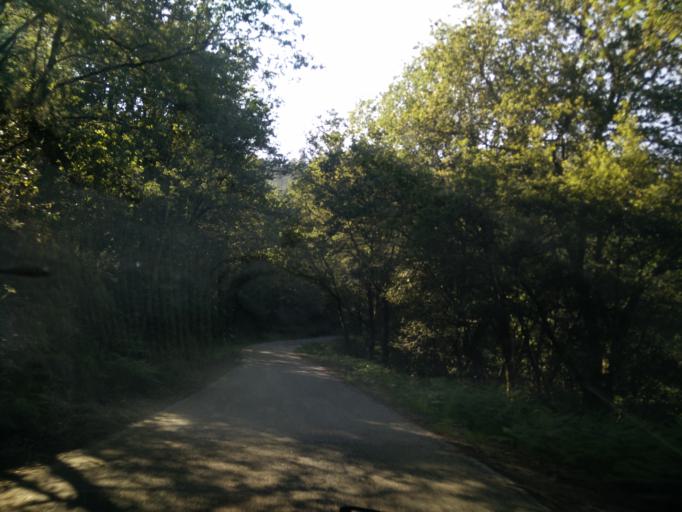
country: ES
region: Galicia
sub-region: Provincia de Pontevedra
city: Mondariz
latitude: 42.2639
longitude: -8.4103
